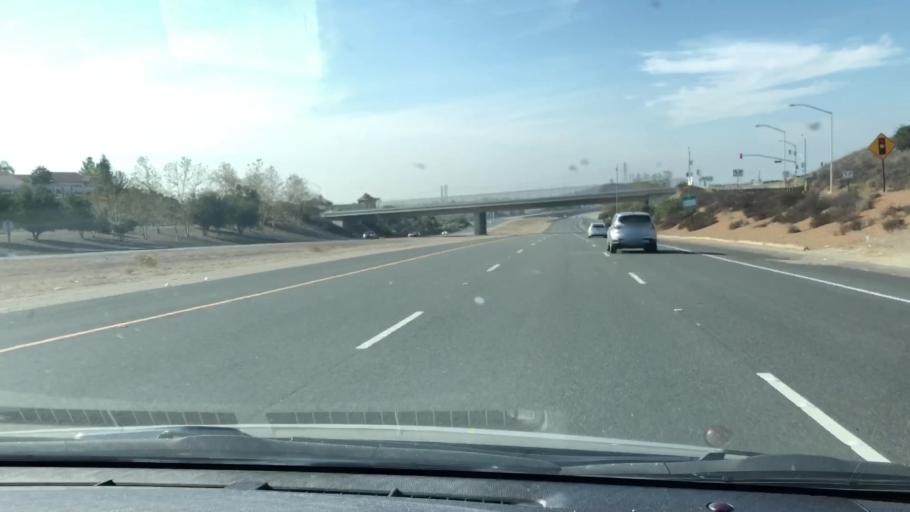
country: US
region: California
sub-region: Orange County
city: Rancho Santa Margarita
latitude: 33.6546
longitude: -117.6229
